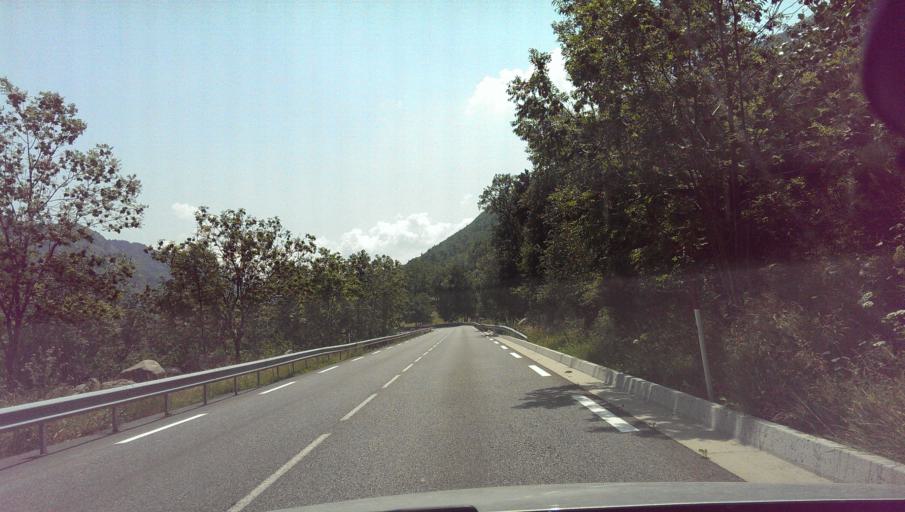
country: ES
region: Catalonia
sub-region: Provincia de Girona
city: Guils de Cerdanya
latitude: 42.5001
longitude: 1.8380
